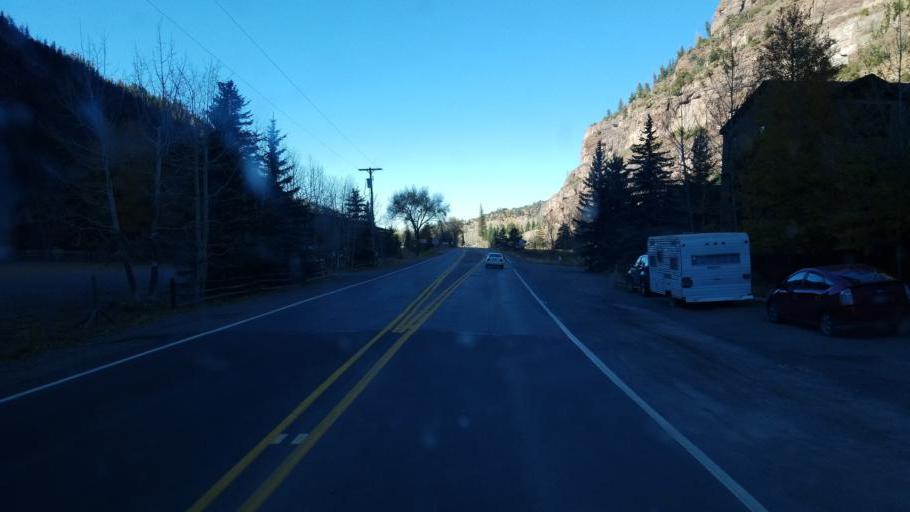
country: US
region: Colorado
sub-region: Ouray County
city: Ouray
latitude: 38.0372
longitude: -107.6783
